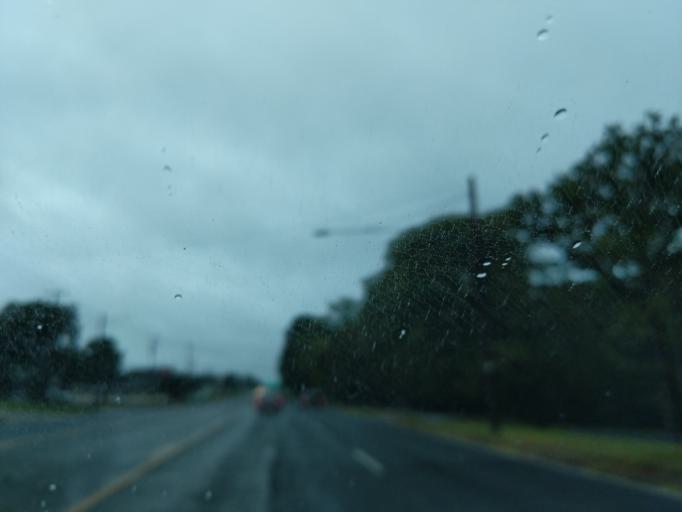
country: US
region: Texas
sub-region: Nacogdoches County
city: Nacogdoches
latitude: 31.6427
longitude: -94.6539
